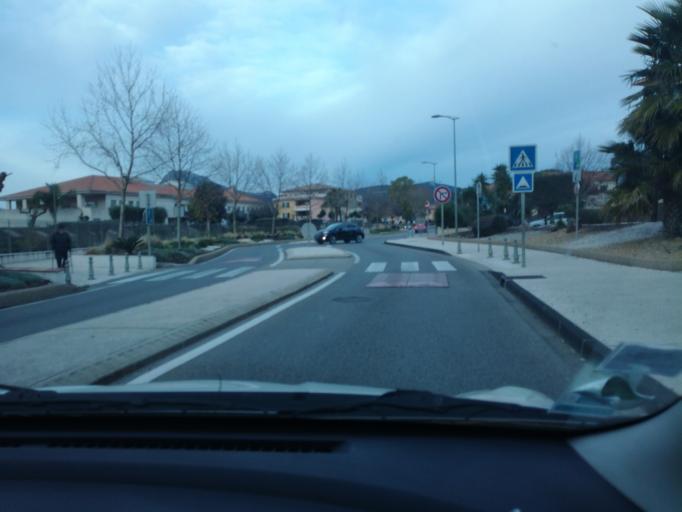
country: FR
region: Provence-Alpes-Cote d'Azur
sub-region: Departement du Var
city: La Crau
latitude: 43.1463
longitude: 6.0780
